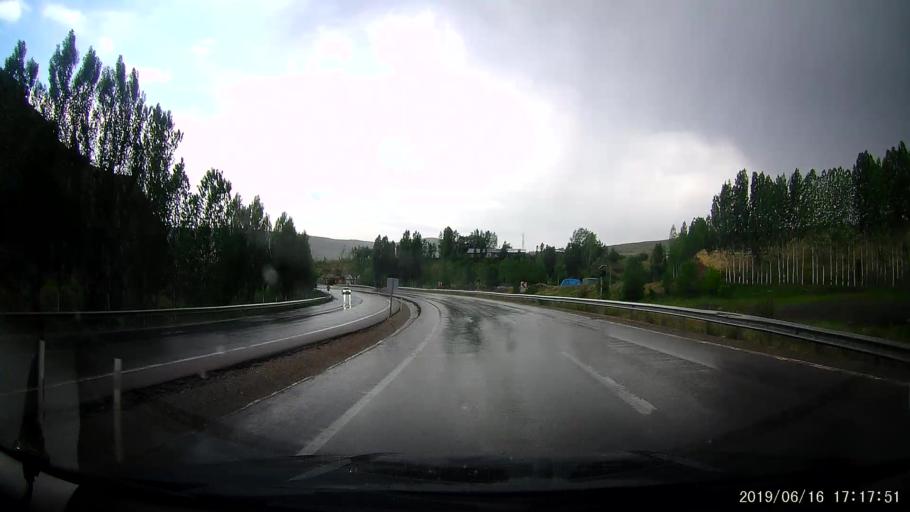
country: TR
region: Erzincan
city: Tercan
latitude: 39.8214
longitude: 40.5303
